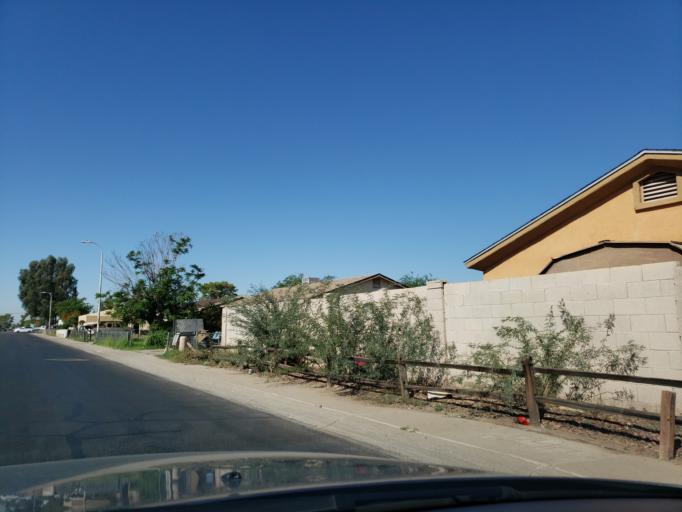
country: US
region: Arizona
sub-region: Maricopa County
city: Glendale
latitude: 33.4767
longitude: -112.2012
